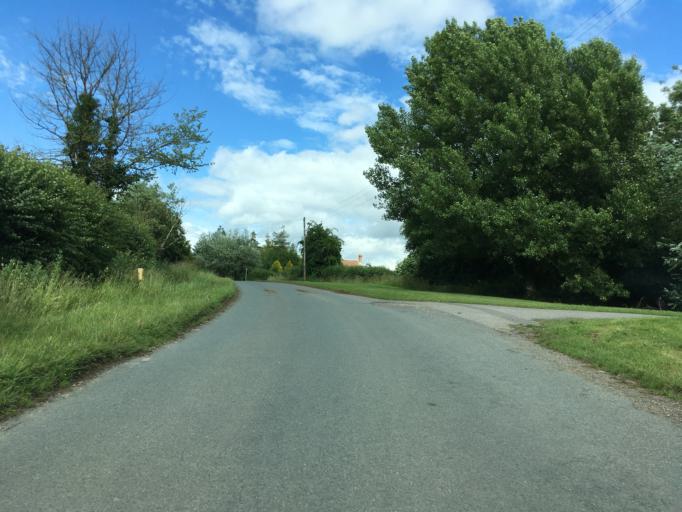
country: GB
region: England
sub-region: Gloucestershire
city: Gloucester
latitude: 51.8335
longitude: -2.3358
